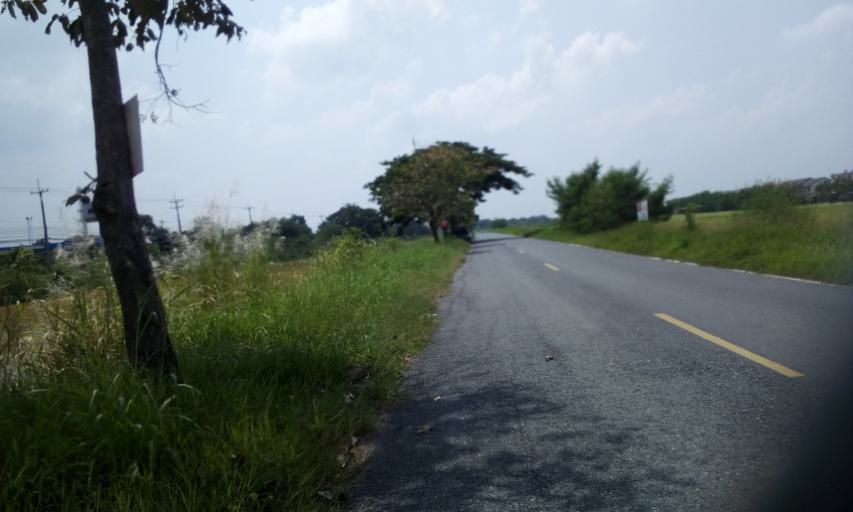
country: TH
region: Pathum Thani
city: Nong Suea
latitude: 14.0666
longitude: 100.8238
